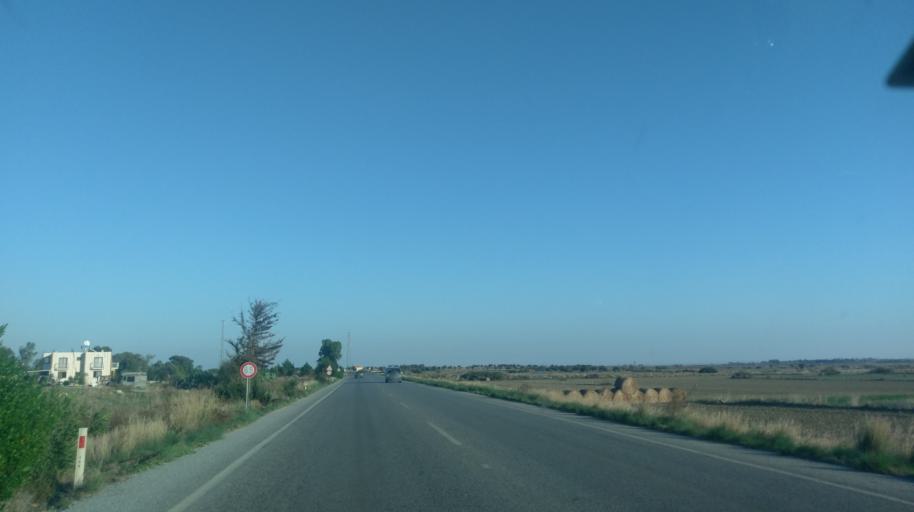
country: CY
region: Ammochostos
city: Lefkonoiko
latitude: 35.2599
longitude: 33.6554
